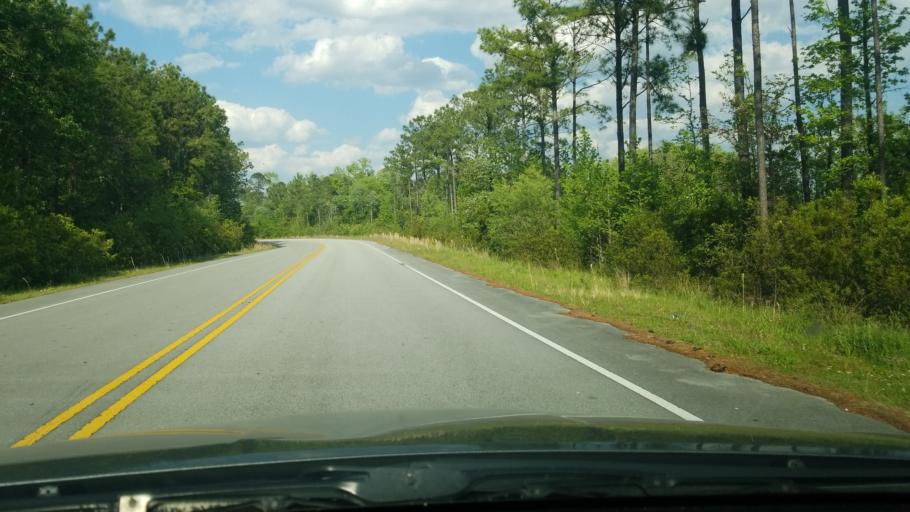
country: US
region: North Carolina
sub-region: Onslow County
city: Pumpkin Center
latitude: 34.7771
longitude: -77.3991
